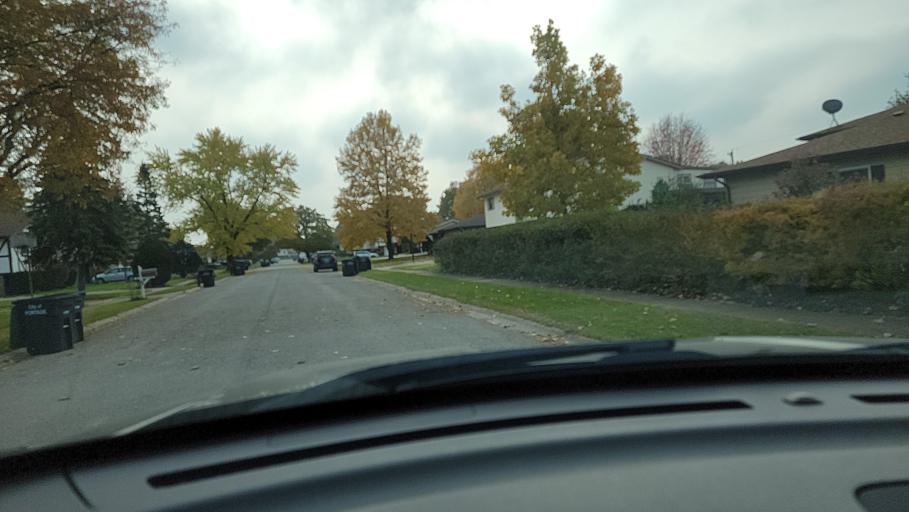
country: US
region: Indiana
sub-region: Porter County
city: Portage
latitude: 41.5930
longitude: -87.1569
